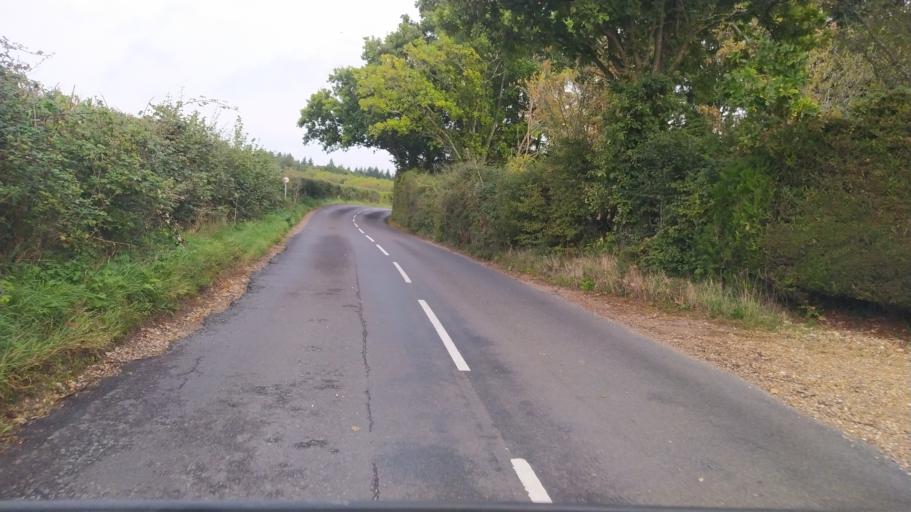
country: GB
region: England
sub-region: Hampshire
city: Romsey
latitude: 51.0287
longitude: -1.5408
